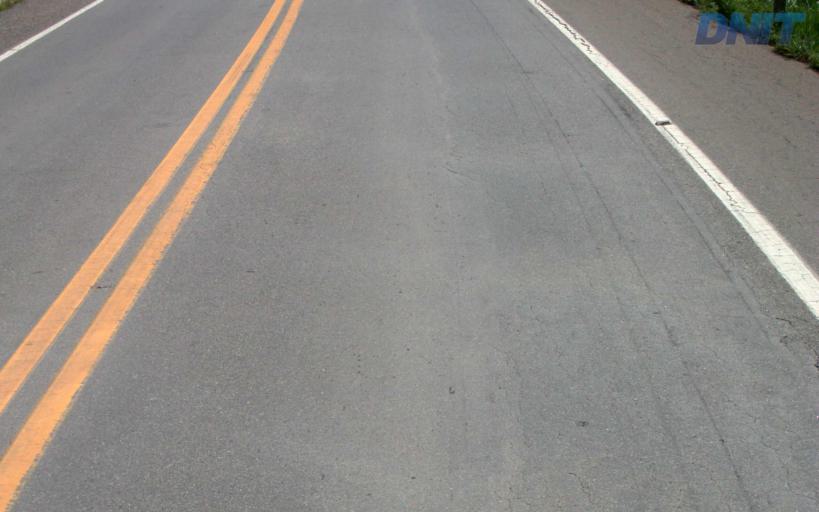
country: BR
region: Minas Gerais
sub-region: Governador Valadares
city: Governador Valadares
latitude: -19.0657
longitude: -42.1638
